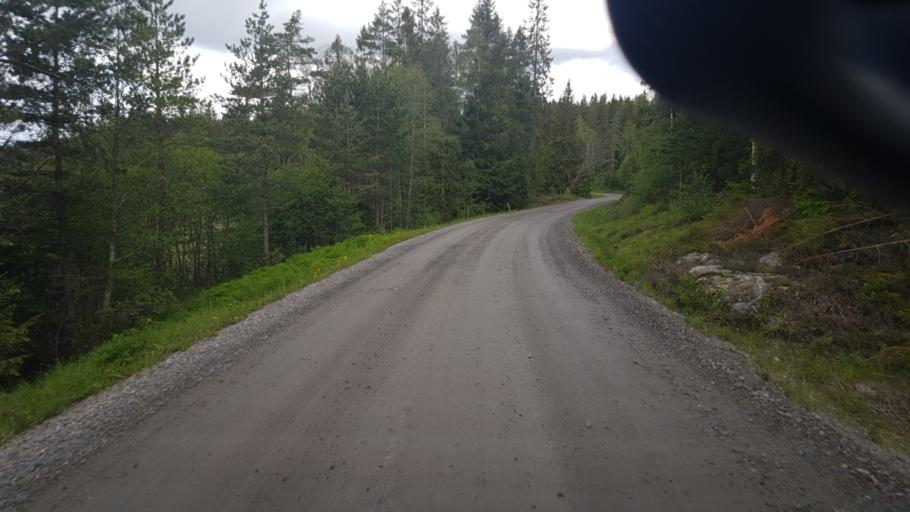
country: NO
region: Ostfold
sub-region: Romskog
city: Romskog
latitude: 59.7093
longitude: 12.0390
